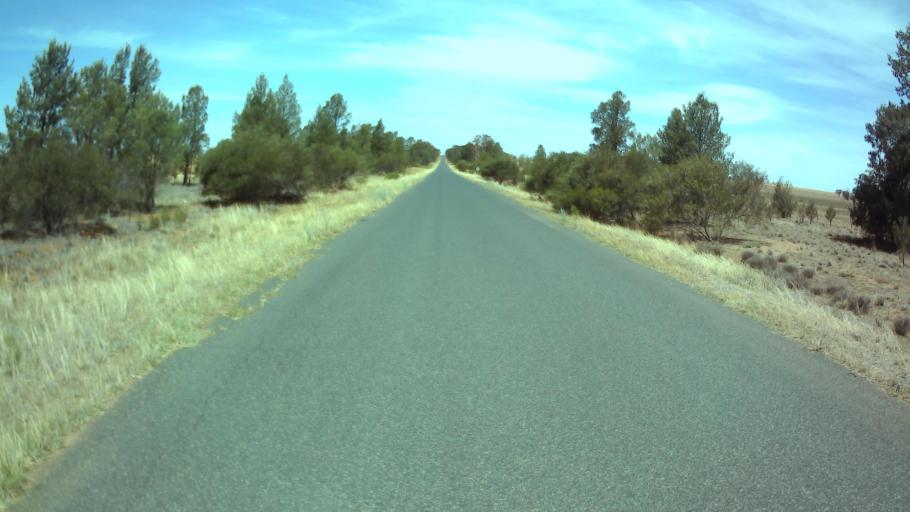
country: AU
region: New South Wales
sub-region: Weddin
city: Grenfell
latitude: -33.8910
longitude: 147.7438
